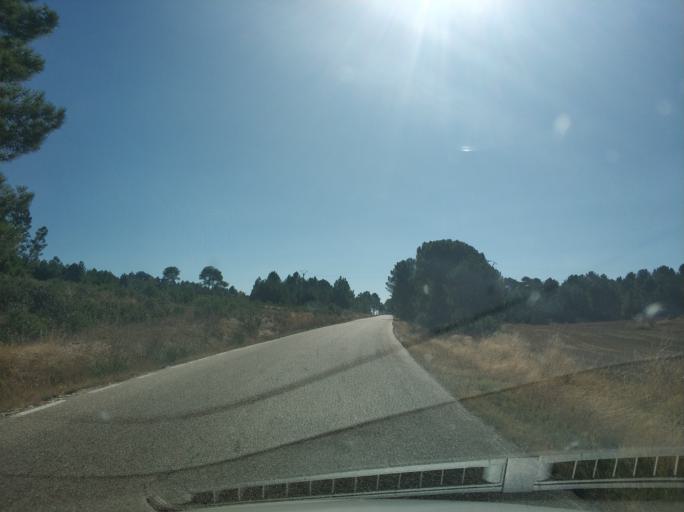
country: ES
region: Castille and Leon
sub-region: Provincia de Soria
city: Santa Maria de las Hoyas
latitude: 41.7779
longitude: -3.1831
